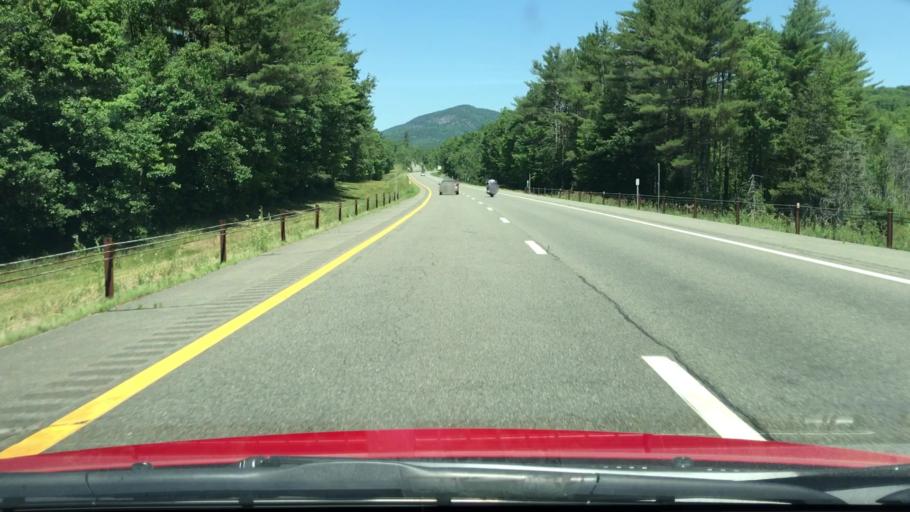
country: US
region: New York
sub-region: Essex County
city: Elizabethtown
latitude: 44.3437
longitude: -73.5326
